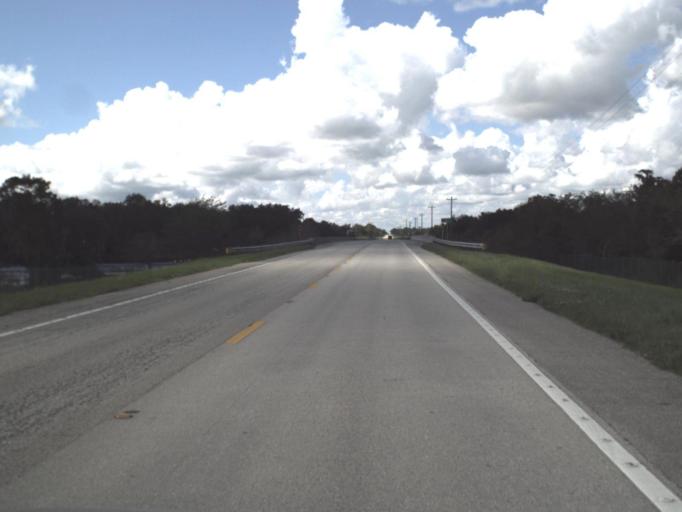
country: US
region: Florida
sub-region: DeSoto County
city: Arcadia
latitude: 27.2547
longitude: -81.9664
